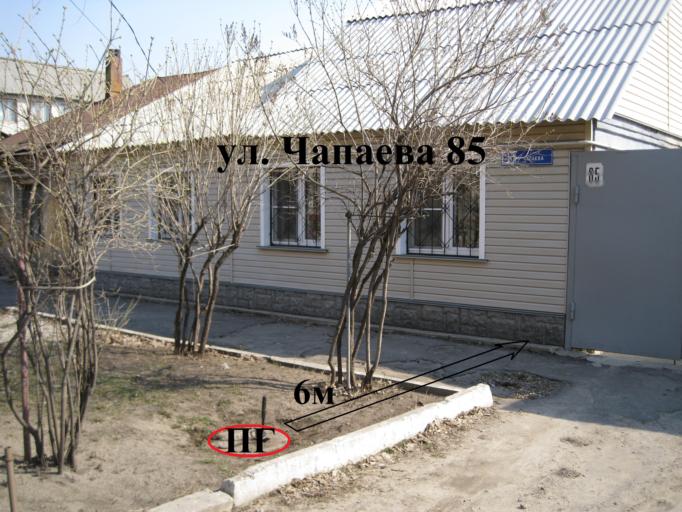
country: RU
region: Voronezj
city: Voronezh
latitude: 51.6360
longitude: 39.1886
